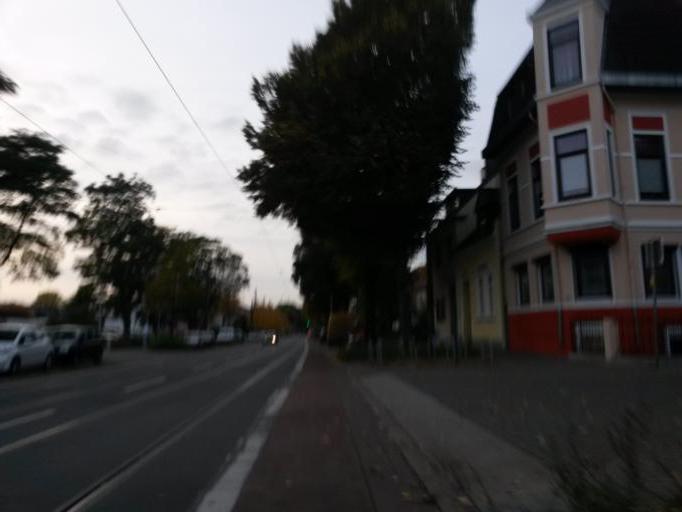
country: DE
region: Bremen
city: Bremen
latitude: 53.0665
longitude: 8.8587
